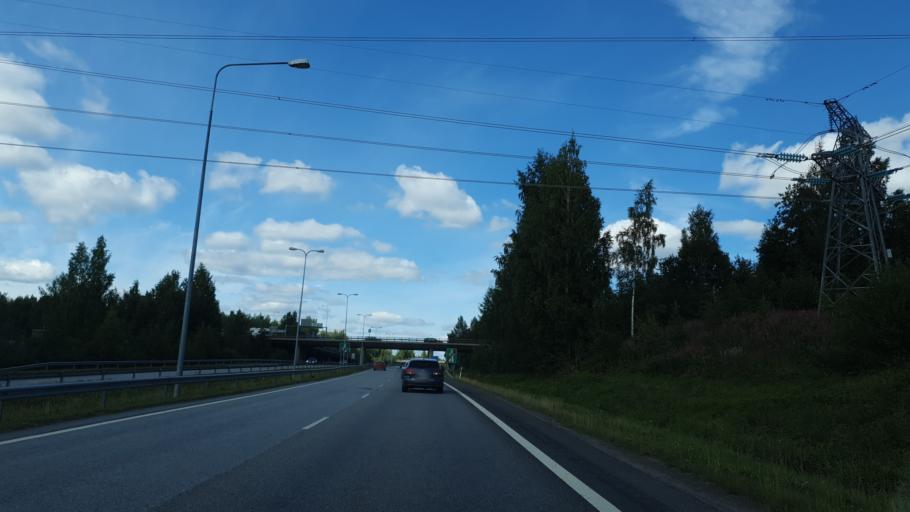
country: FI
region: Central Finland
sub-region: Jyvaeskylae
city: Jyvaeskylae
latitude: 62.2163
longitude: 25.7253
